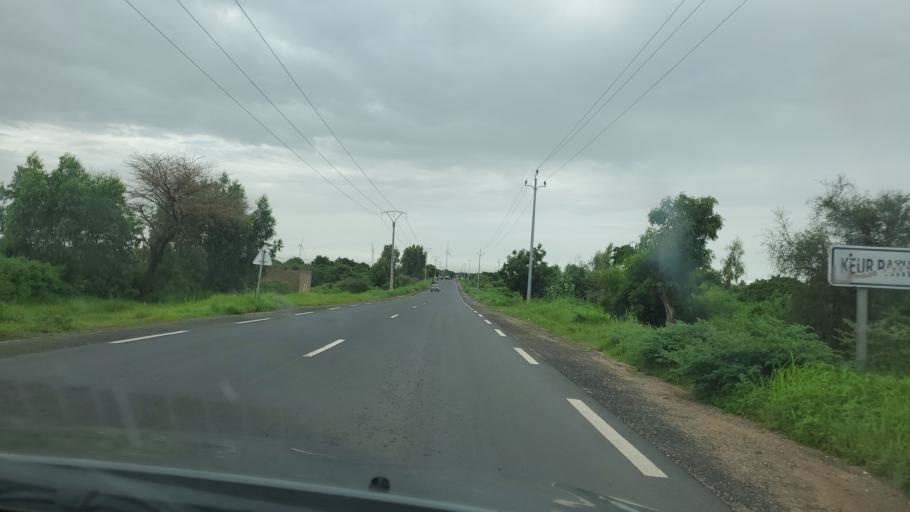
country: SN
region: Thies
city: Kayar
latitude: 15.0990
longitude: -16.9129
